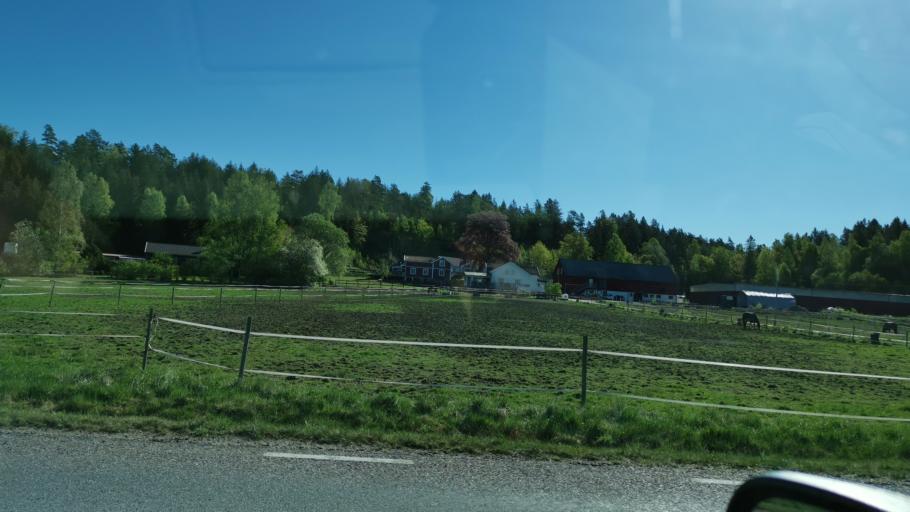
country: SE
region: Vaestra Goetaland
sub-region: Uddevalla Kommun
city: Uddevalla
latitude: 58.2925
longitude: 11.8985
